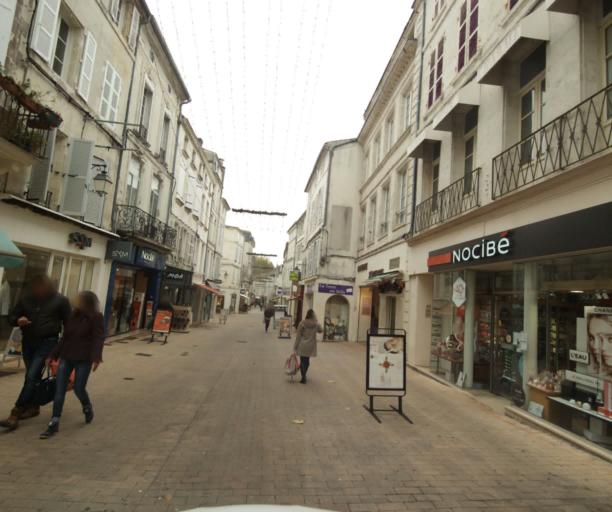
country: FR
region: Poitou-Charentes
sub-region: Departement de la Charente-Maritime
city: Saintes
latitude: 45.7467
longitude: -0.6335
